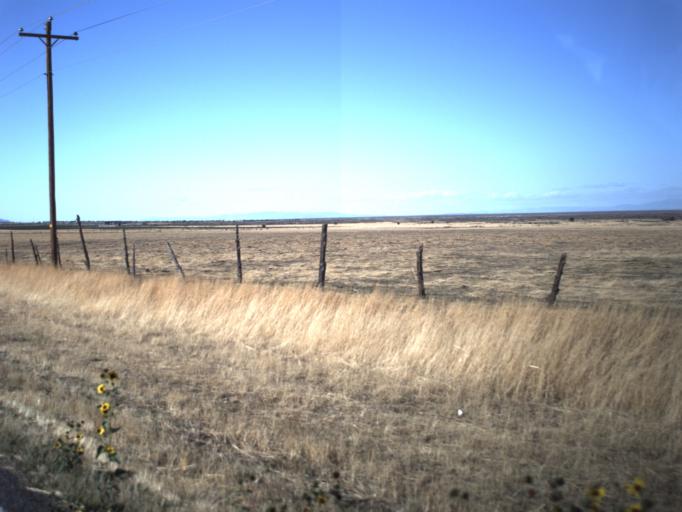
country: US
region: Utah
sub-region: Millard County
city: Delta
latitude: 39.4252
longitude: -112.3266
